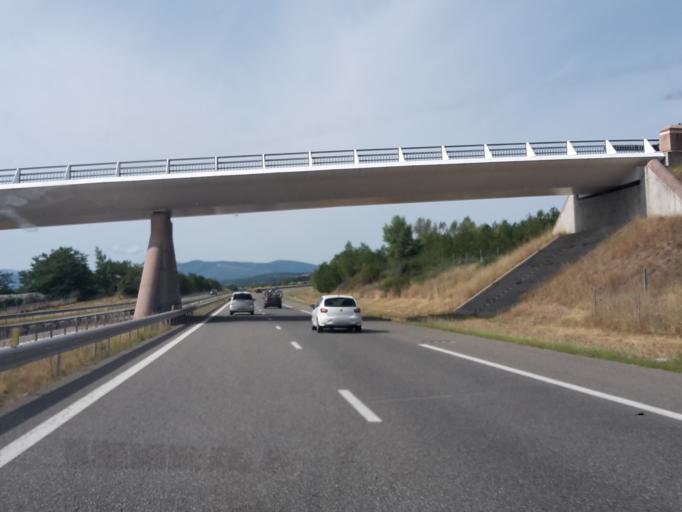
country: FR
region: Provence-Alpes-Cote d'Azur
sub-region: Departement des Hautes-Alpes
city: Tallard
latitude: 44.4065
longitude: 5.9570
